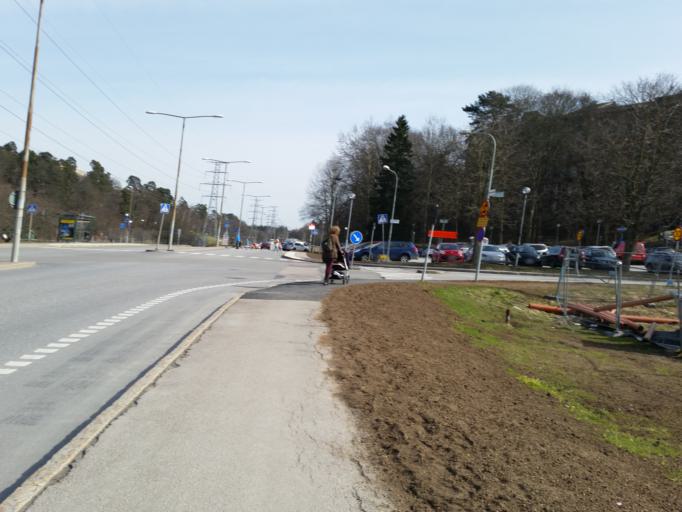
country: SE
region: Stockholm
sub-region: Norrtalje Kommun
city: Bergshamra
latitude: 59.3704
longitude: 18.0526
